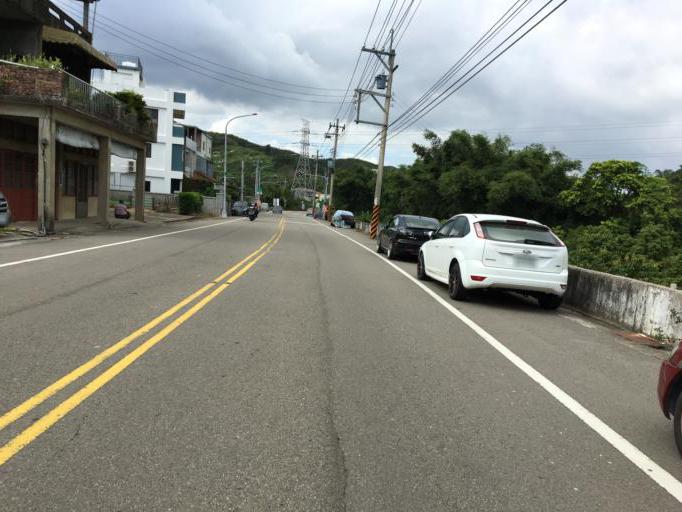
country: TW
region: Taiwan
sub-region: Hsinchu
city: Hsinchu
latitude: 24.6977
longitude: 120.9620
